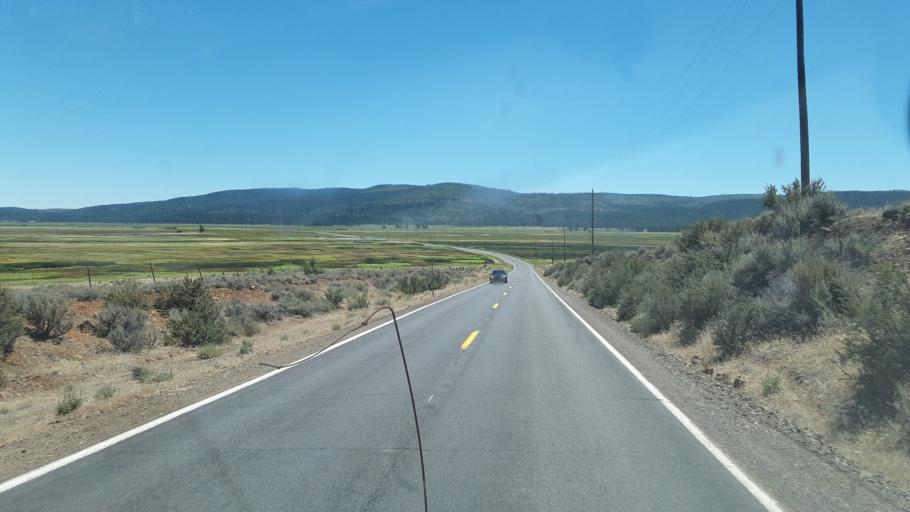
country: US
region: California
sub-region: Lassen County
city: Susanville
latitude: 40.5706
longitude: -120.6421
